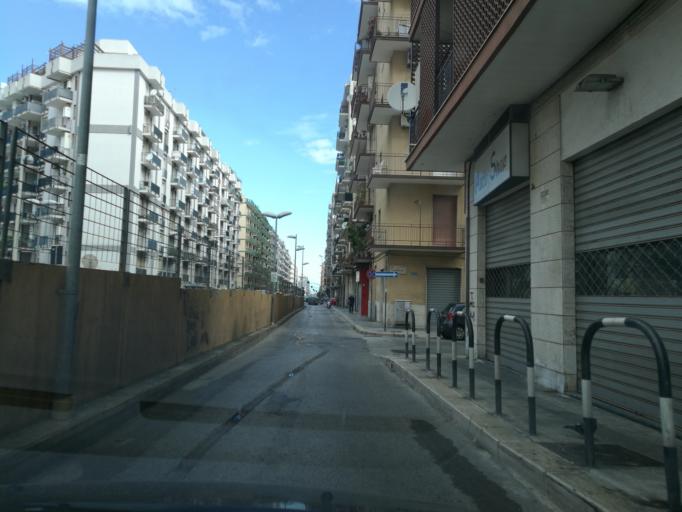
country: IT
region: Apulia
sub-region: Provincia di Bari
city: Bari
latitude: 41.1185
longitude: 16.8522
